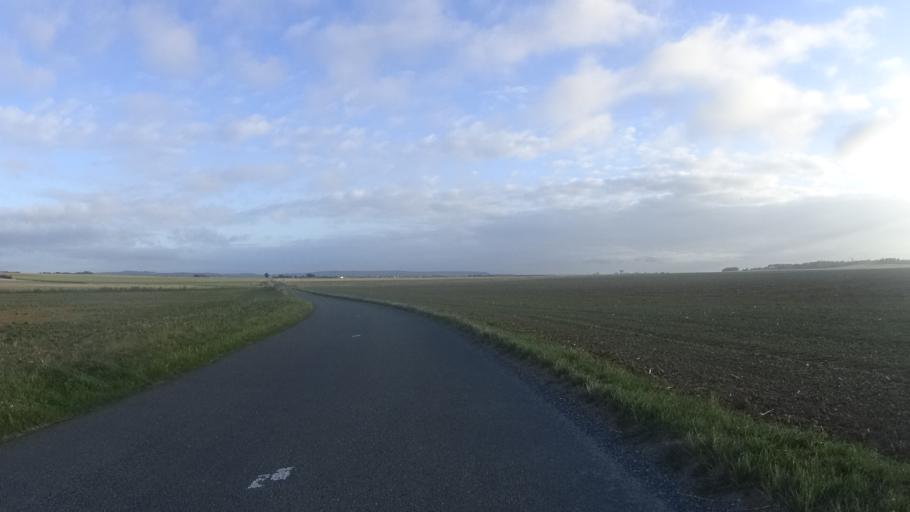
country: FR
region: Picardie
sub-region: Departement de l'Oise
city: Chamant
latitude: 49.1892
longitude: 2.6719
